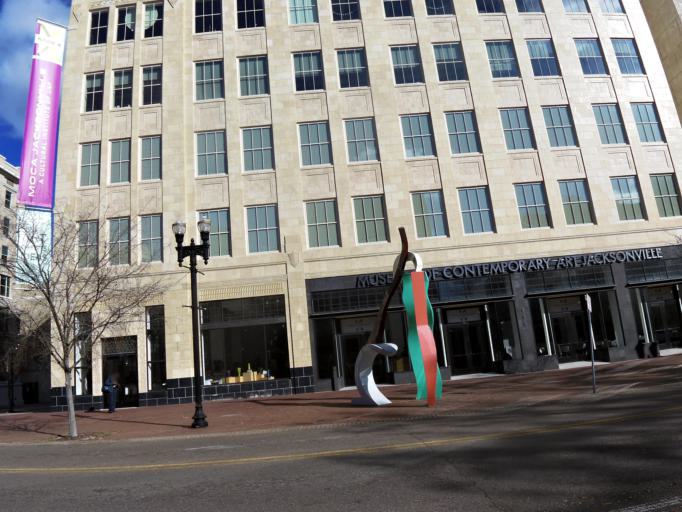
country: US
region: Florida
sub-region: Duval County
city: Jacksonville
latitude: 30.3294
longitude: -81.6587
